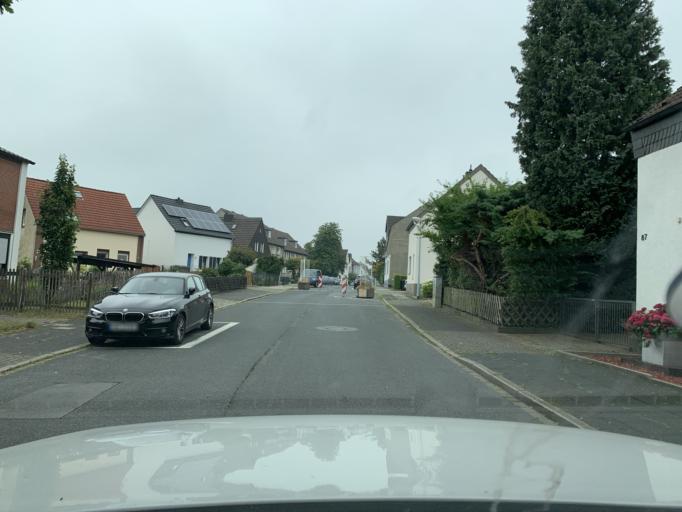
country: DE
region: North Rhine-Westphalia
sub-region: Regierungsbezirk Dusseldorf
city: Muelheim (Ruhr)
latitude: 51.4037
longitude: 6.8664
